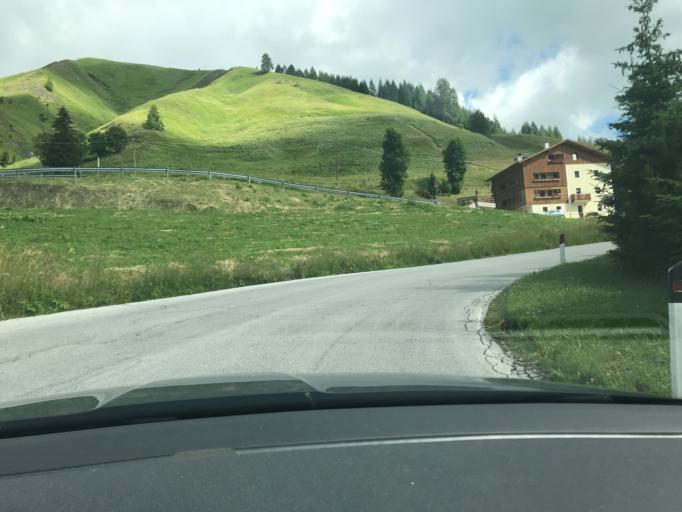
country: IT
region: Trentino-Alto Adige
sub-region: Bolzano
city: Corvara in Badia
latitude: 46.4949
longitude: 11.8667
